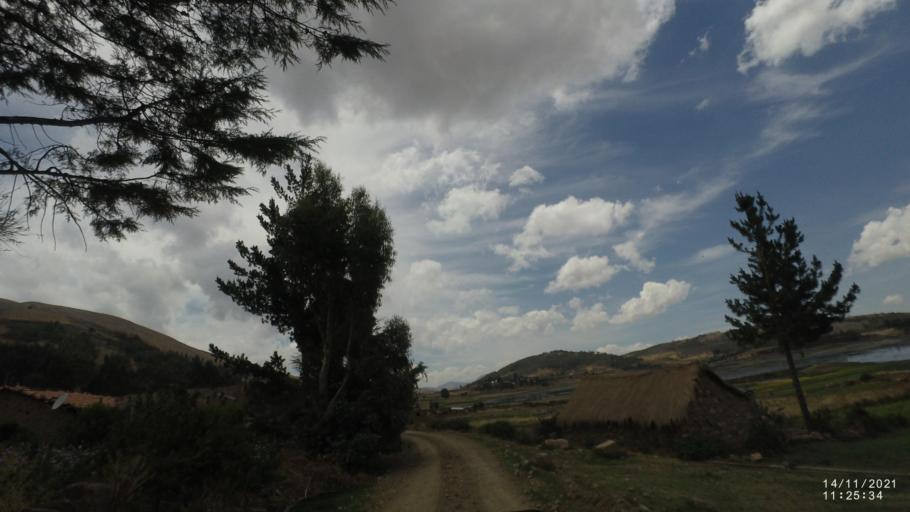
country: BO
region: Cochabamba
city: Cochabamba
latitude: -17.3362
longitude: -66.0219
